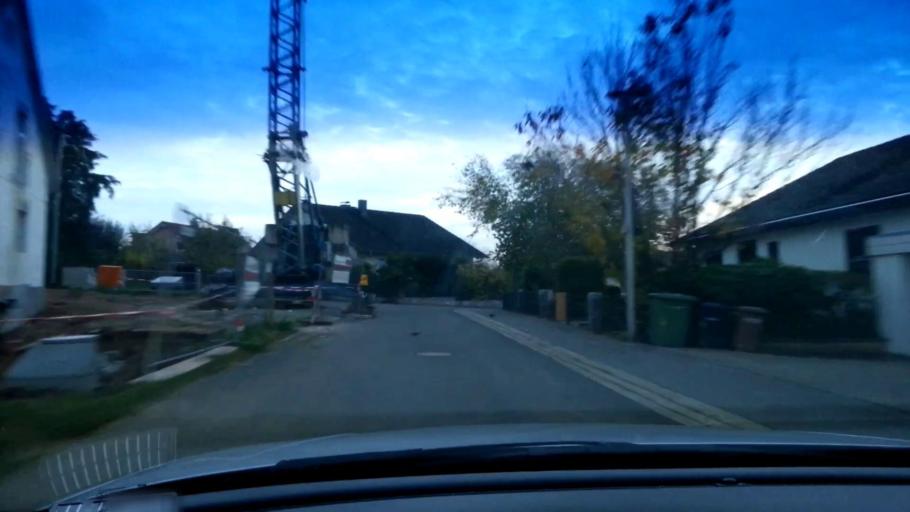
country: DE
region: Bavaria
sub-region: Upper Franconia
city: Breitengussbach
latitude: 49.9777
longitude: 10.8950
